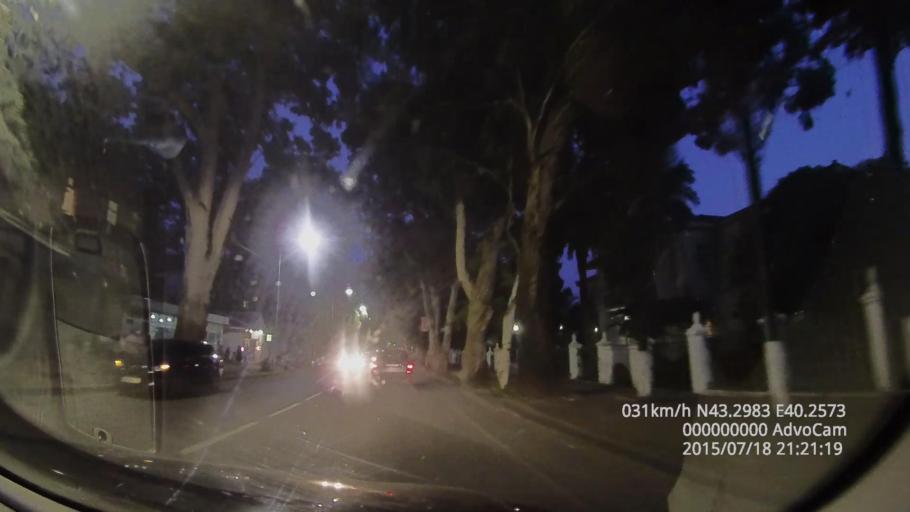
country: GE
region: Abkhazia
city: Gagra
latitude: 43.2981
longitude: 40.2574
